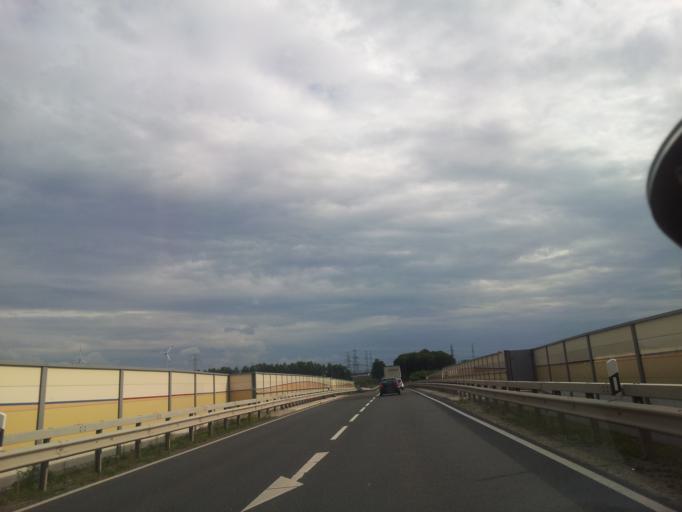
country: DE
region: Saxony-Anhalt
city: Colbitz
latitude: 52.2859
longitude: 11.6240
